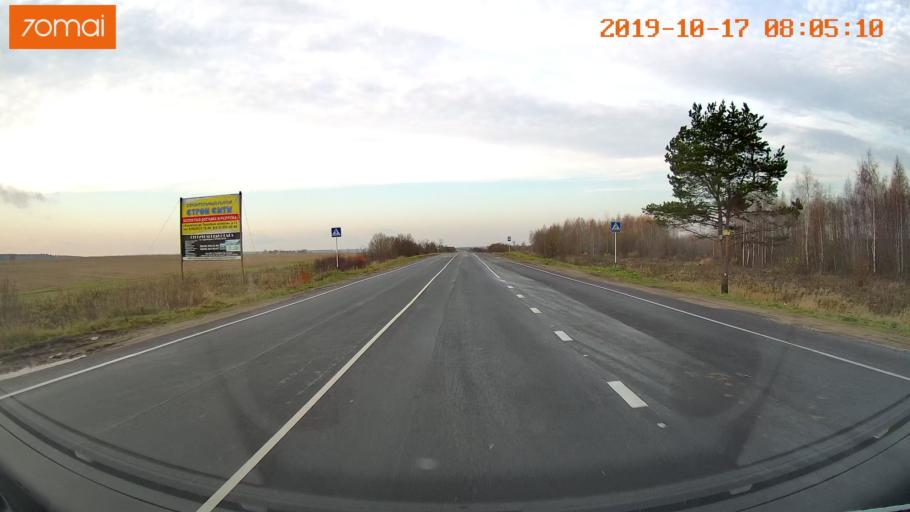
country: RU
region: Vladimir
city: Kol'chugino
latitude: 56.3375
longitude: 39.4209
